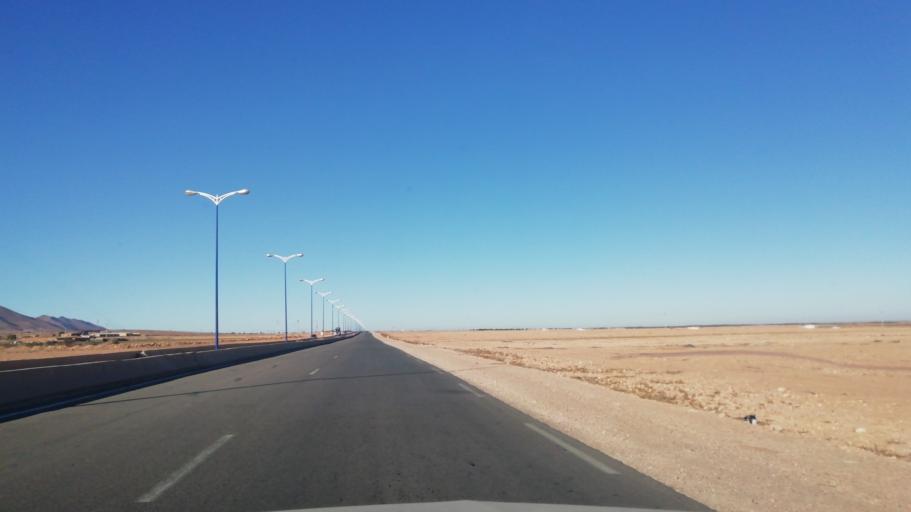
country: DZ
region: Wilaya de Naama
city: Naama
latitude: 33.5725
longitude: -0.2405
